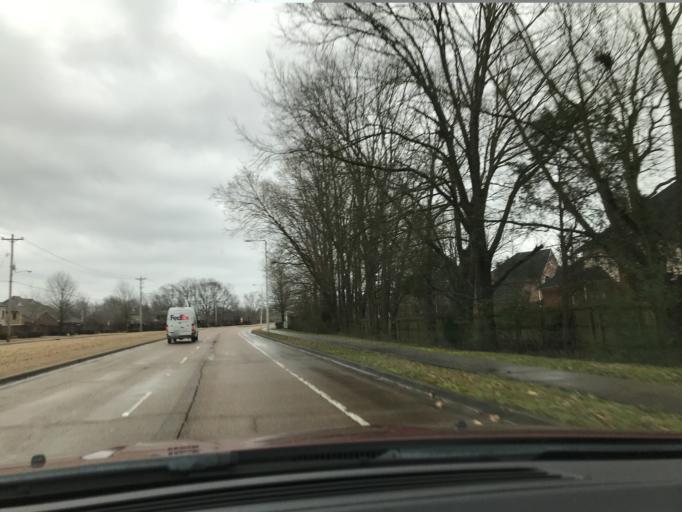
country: US
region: Tennessee
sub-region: Shelby County
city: Collierville
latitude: 35.0850
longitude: -89.6867
